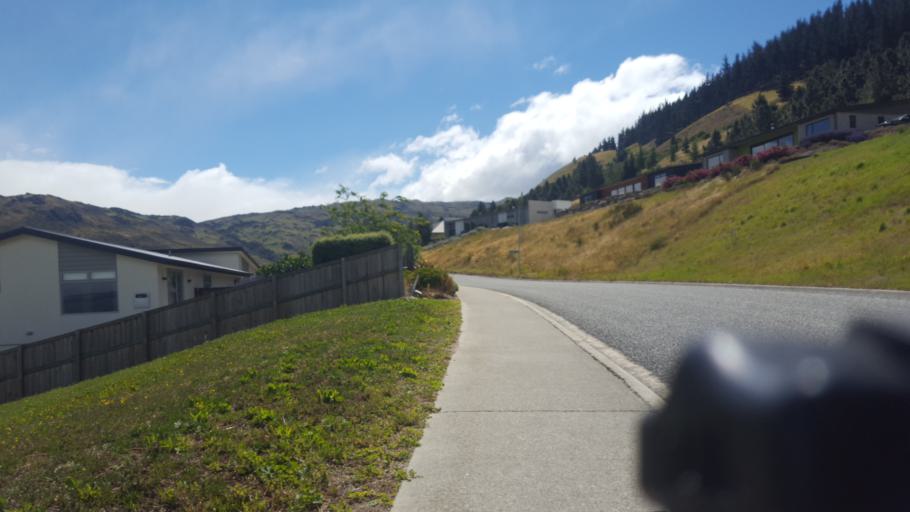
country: NZ
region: Otago
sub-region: Queenstown-Lakes District
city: Wanaka
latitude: -45.1873
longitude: 169.3253
